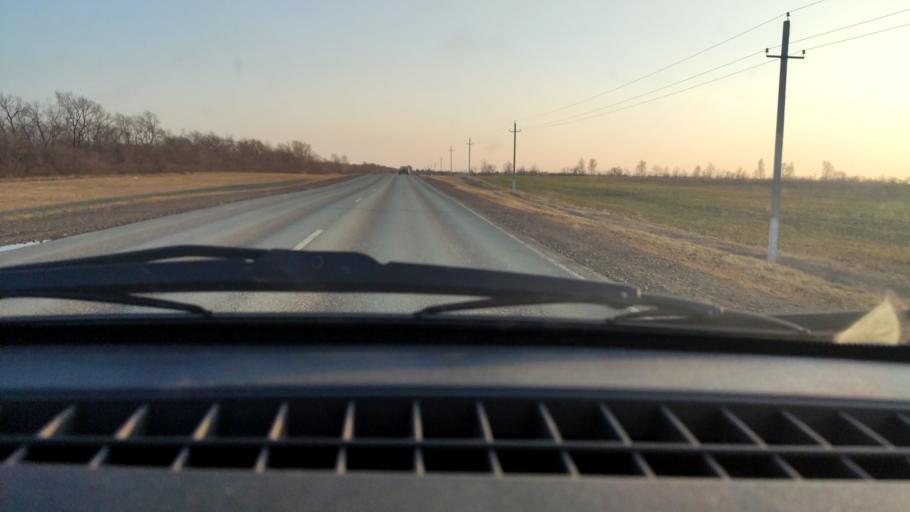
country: RU
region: Bashkortostan
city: Davlekanovo
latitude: 54.3076
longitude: 55.1404
